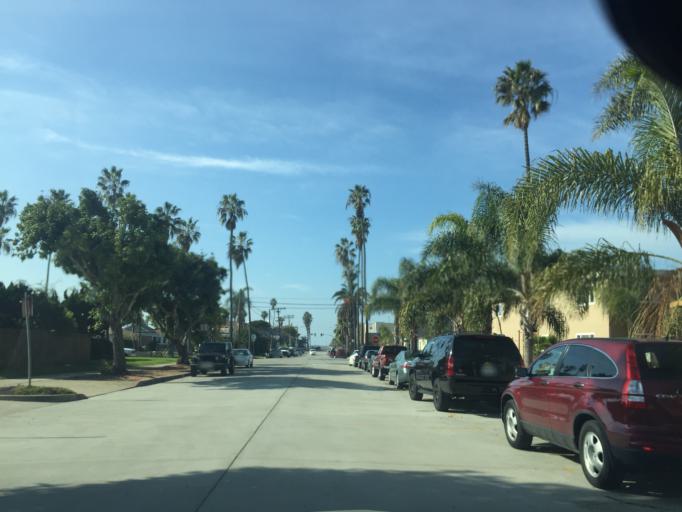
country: US
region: California
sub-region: San Diego County
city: La Jolla
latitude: 32.7933
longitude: -117.2518
